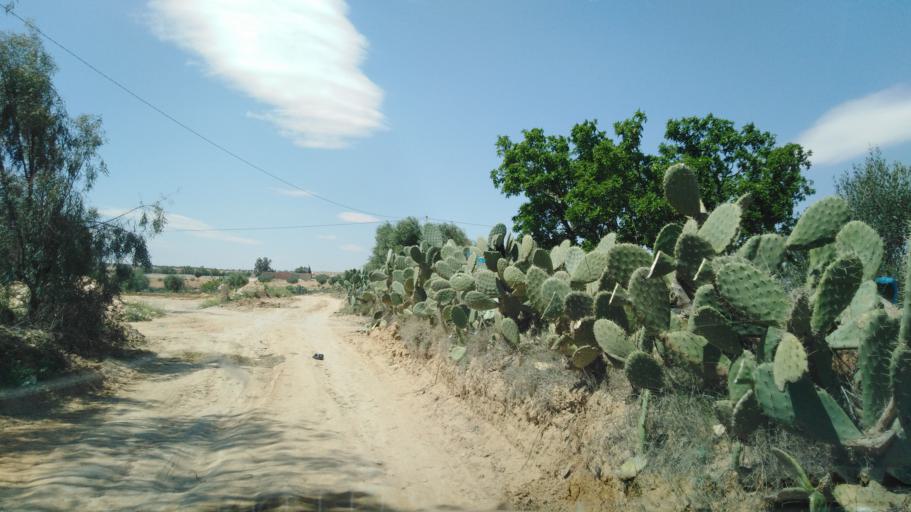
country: TN
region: Safaqis
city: Sfax
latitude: 34.7640
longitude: 10.5187
